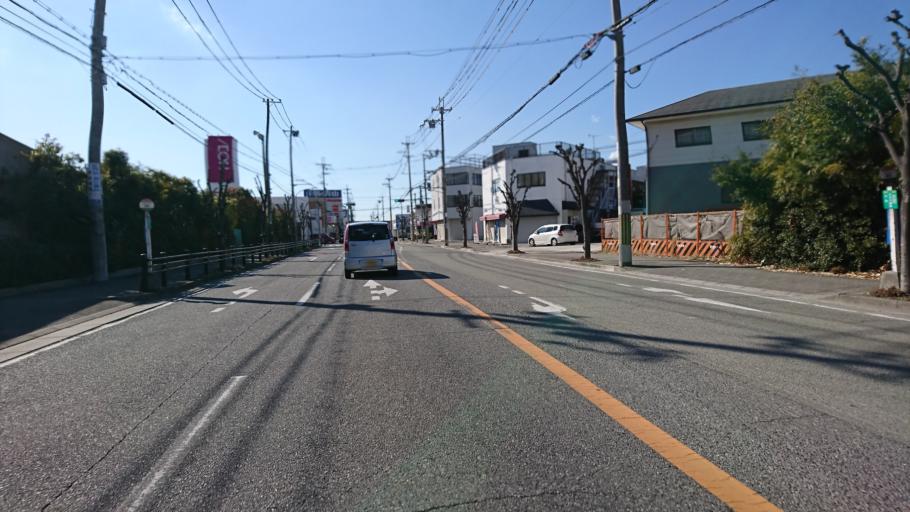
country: JP
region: Hyogo
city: Kakogawacho-honmachi
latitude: 34.7697
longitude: 134.8018
